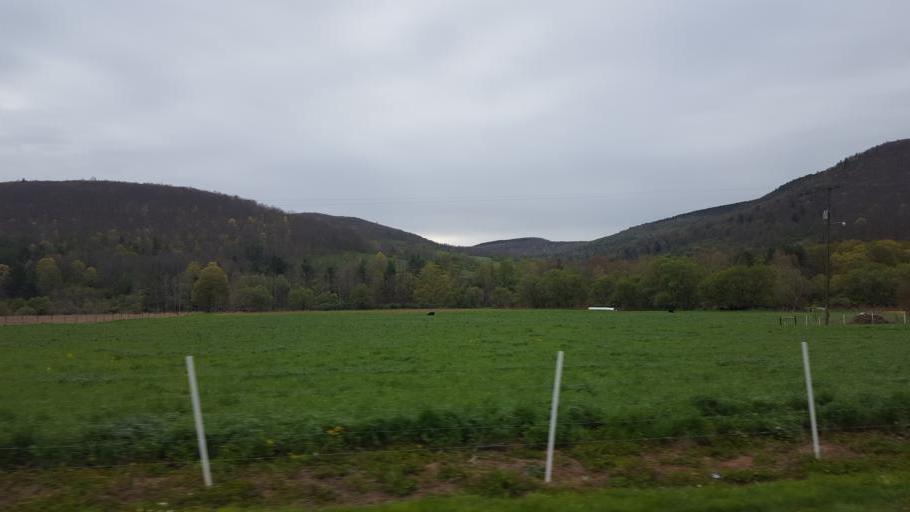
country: US
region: Pennsylvania
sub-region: Tioga County
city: Westfield
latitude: 41.9747
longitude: -77.4622
